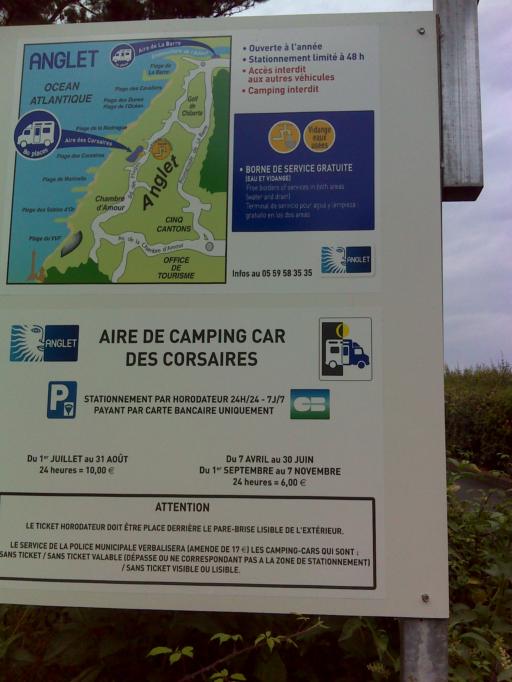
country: FR
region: Aquitaine
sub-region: Departement des Pyrenees-Atlantiques
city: Biarritz
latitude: 43.5069
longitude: -1.5338
